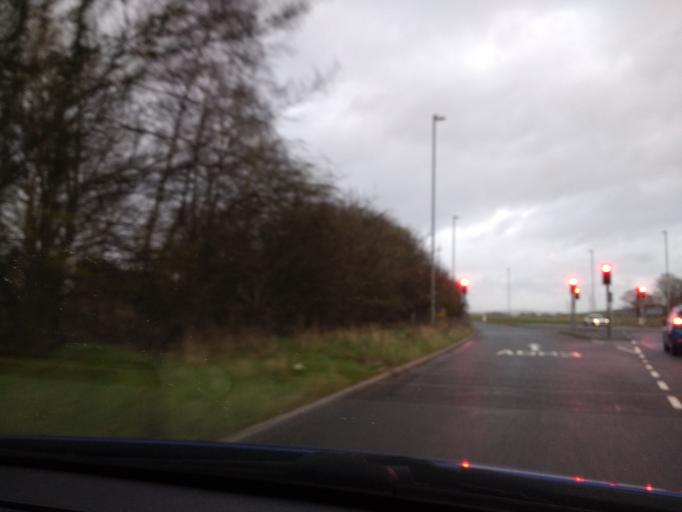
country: GB
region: England
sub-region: Lancashire
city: Bolton le Sands
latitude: 54.0721
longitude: -2.7626
